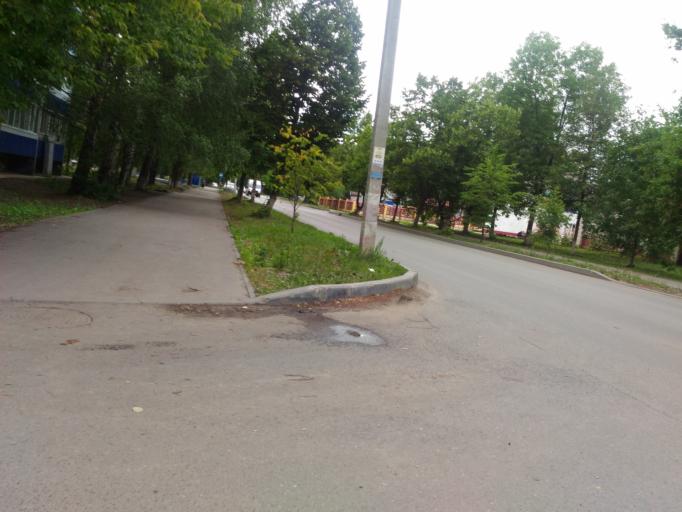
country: RU
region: Ulyanovsk
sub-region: Ulyanovskiy Rayon
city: Ulyanovsk
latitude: 54.2827
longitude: 48.2906
